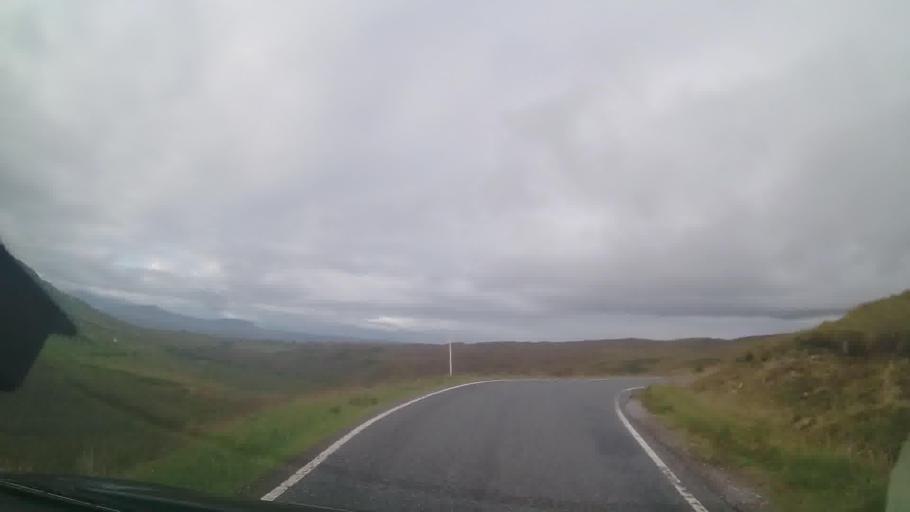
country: GB
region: Scotland
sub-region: Argyll and Bute
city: Isle Of Mull
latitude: 56.7278
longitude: -6.0367
